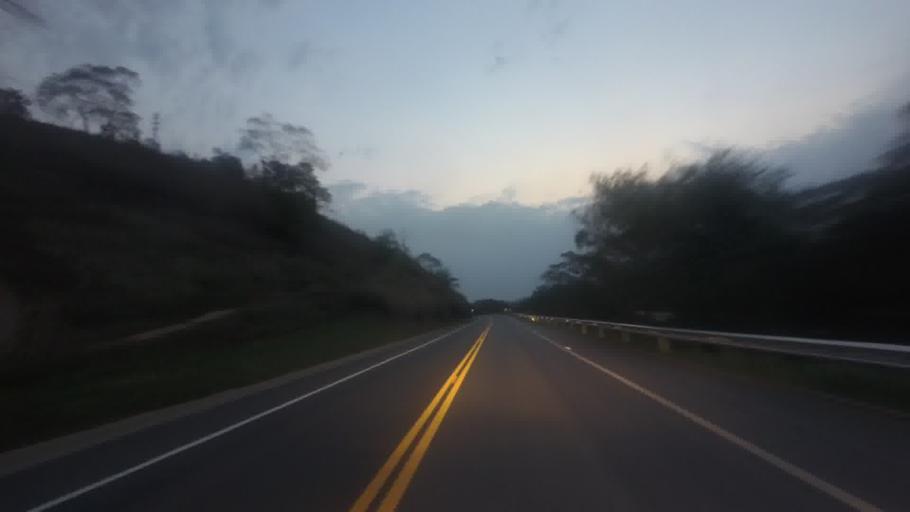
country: BR
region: Minas Gerais
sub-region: Alem Paraiba
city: Alem Paraiba
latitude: -21.9202
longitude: -42.7636
